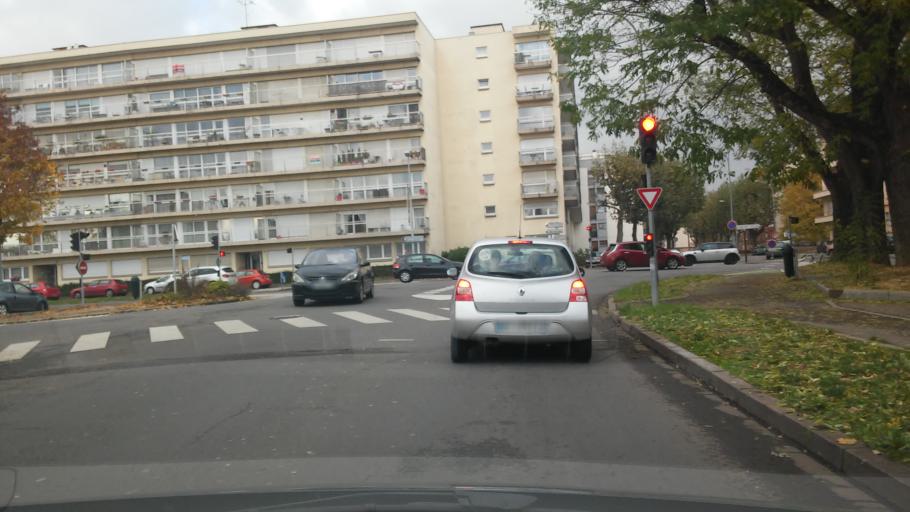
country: FR
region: Lorraine
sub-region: Departement de la Moselle
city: Thionville
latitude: 49.3540
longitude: 6.1588
